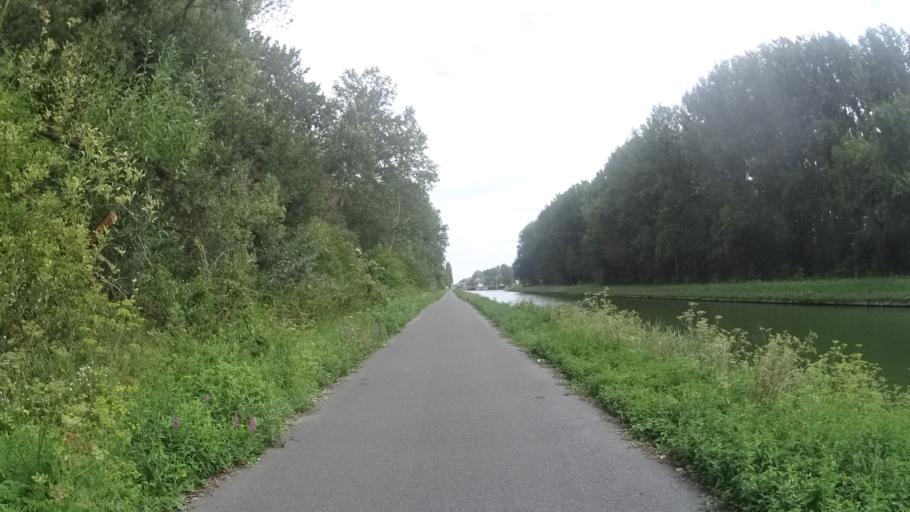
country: FR
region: Picardie
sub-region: Departement de l'Aisne
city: Blerancourt
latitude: 49.5775
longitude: 3.1036
